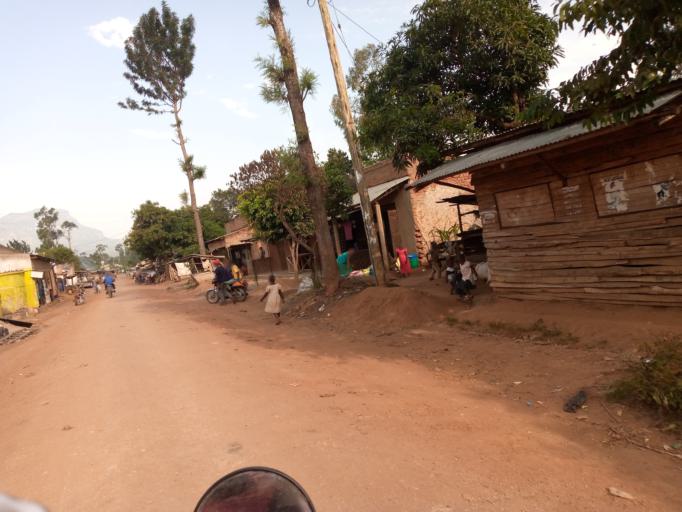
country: UG
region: Eastern Region
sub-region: Mbale District
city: Mbale
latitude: 1.0568
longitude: 34.1599
